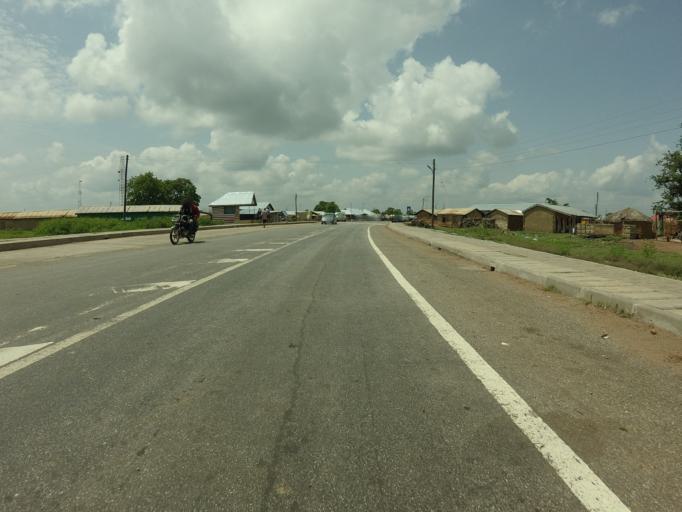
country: GH
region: Northern
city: Tamale
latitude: 9.1242
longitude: -1.2739
